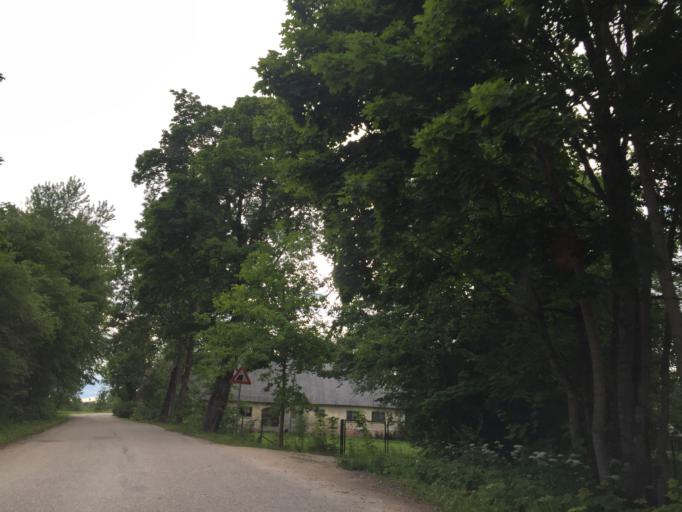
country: LV
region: Amatas Novads
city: Drabesi
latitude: 57.2429
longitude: 25.2092
